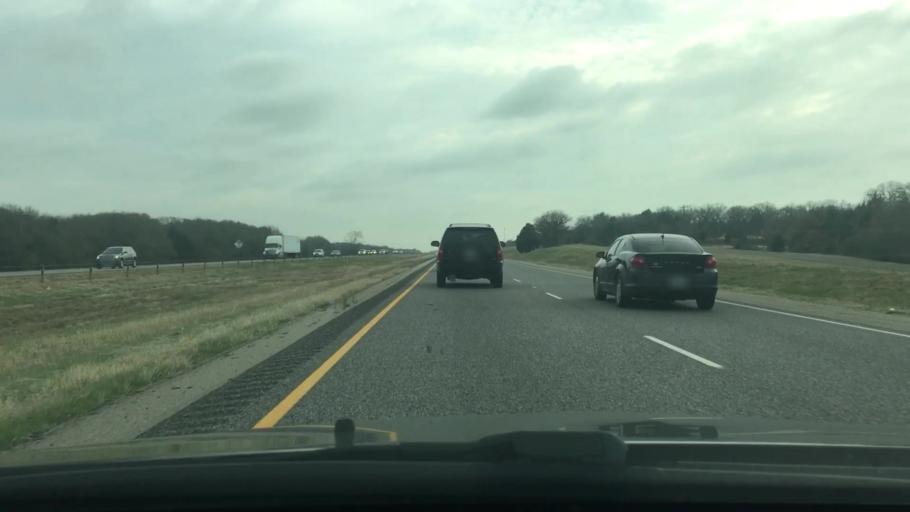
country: US
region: Texas
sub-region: Freestone County
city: Fairfield
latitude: 31.6245
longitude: -96.1576
